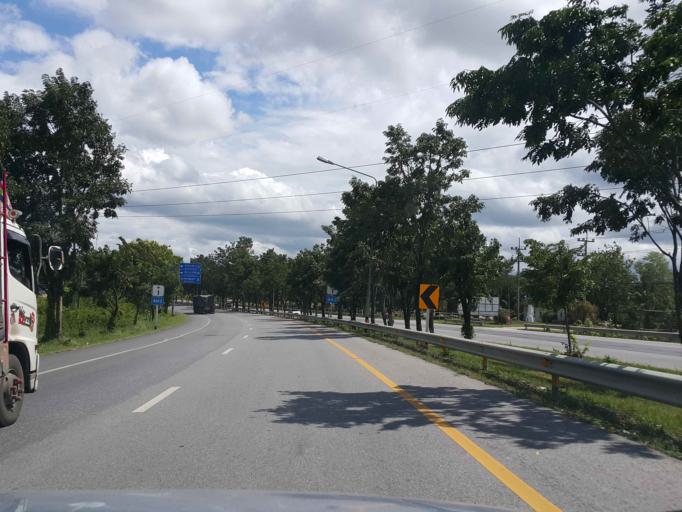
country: TH
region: Tak
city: Tak
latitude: 16.8475
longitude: 99.1117
